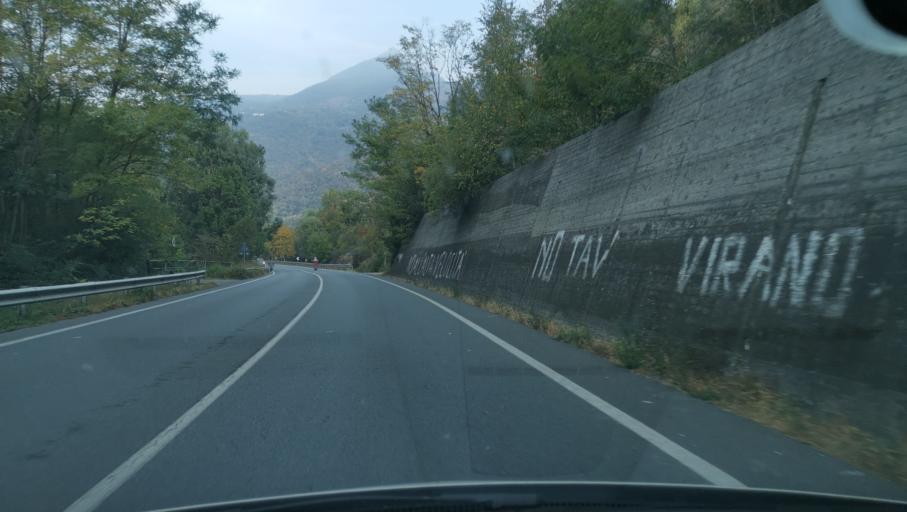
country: IT
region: Piedmont
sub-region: Provincia di Torino
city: Sant'Ambrogio di Torino
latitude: 45.1084
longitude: 7.3705
